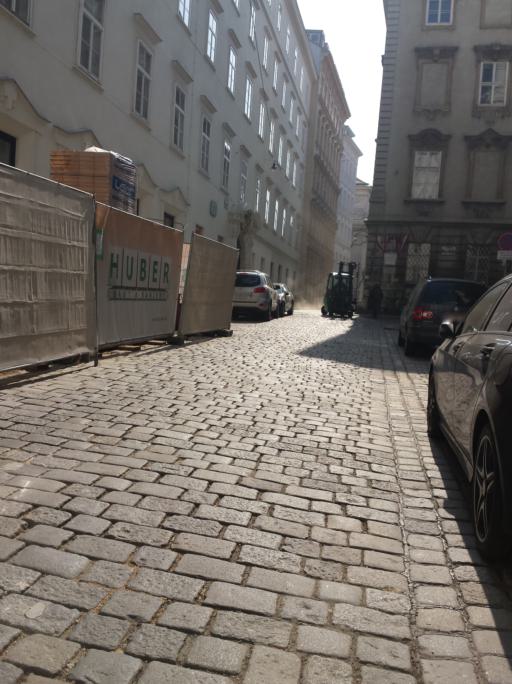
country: AT
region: Vienna
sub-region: Wien Stadt
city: Vienna
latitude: 48.2080
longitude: 16.3757
